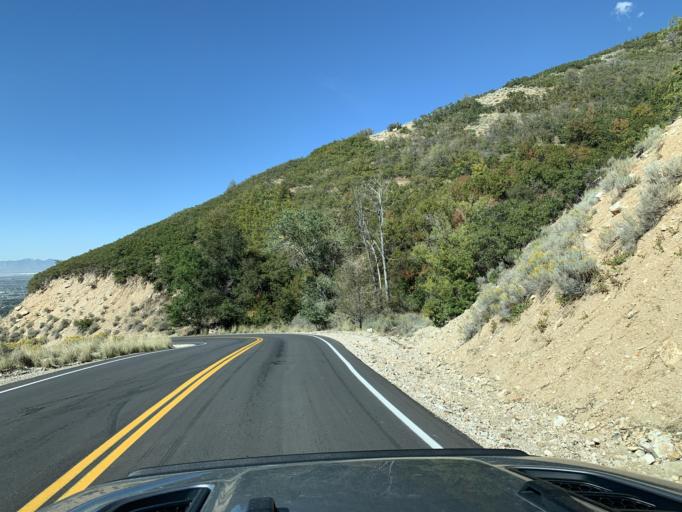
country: US
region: Utah
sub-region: Weber County
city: North Ogden
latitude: 41.3120
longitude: -111.9206
